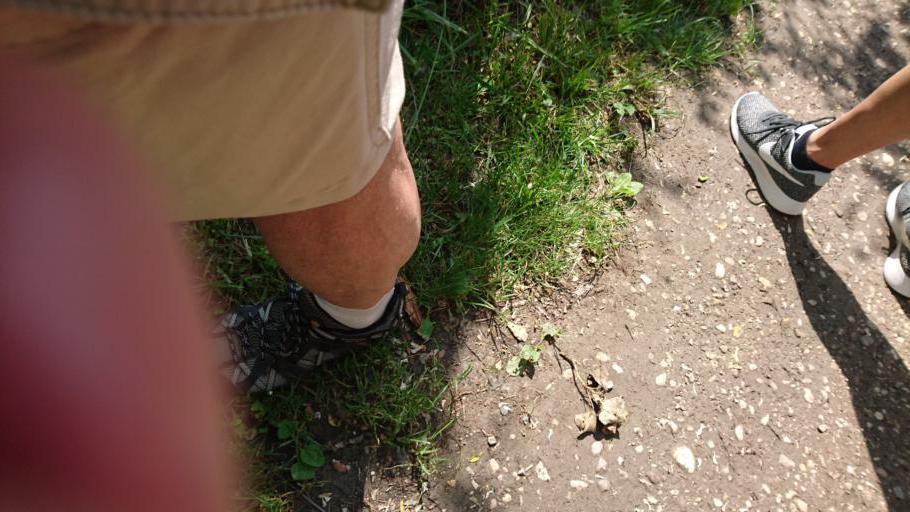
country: IT
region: Veneto
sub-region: Provincia di Venezia
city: Campagna Lupia
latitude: 45.3626
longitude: 12.1378
